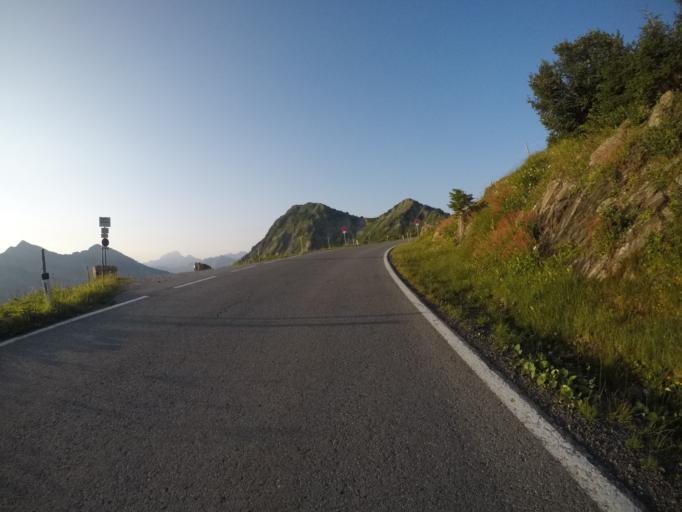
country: AT
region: Vorarlberg
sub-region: Politischer Bezirk Bludenz
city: Blons
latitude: 47.2729
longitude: 9.8349
